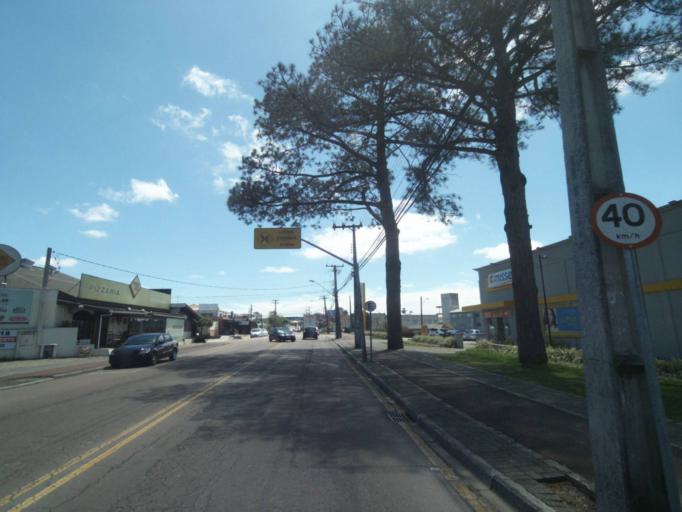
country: BR
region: Parana
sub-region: Curitiba
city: Curitiba
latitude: -25.3856
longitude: -49.2616
